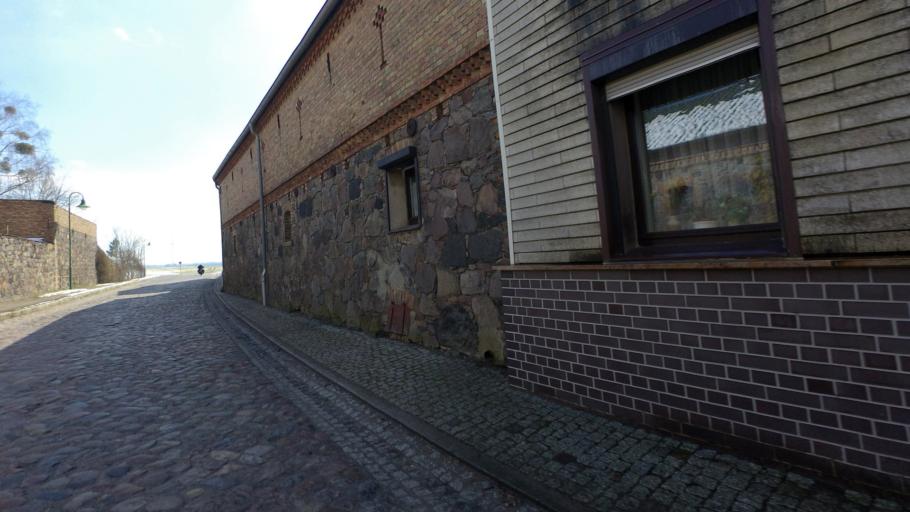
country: DE
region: Brandenburg
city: Werftpfuhl
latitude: 52.6986
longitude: 13.8172
